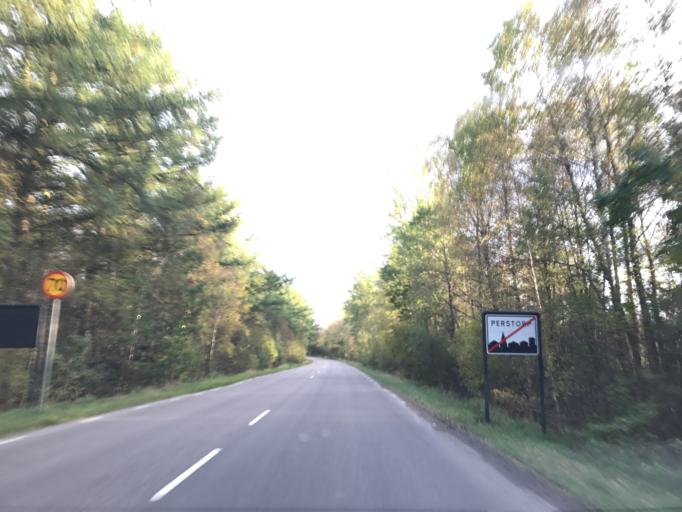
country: SE
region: Skane
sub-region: Perstorps Kommun
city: Perstorp
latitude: 56.1290
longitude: 13.4000
